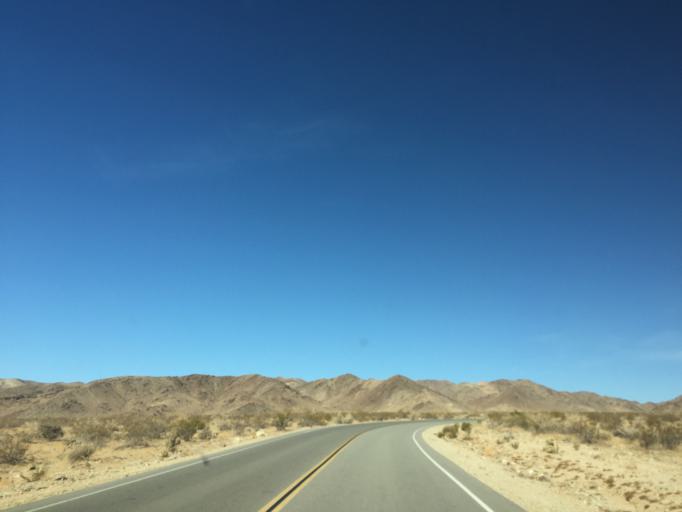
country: US
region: California
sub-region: San Bernardino County
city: Twentynine Palms
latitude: 33.9270
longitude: -115.9394
